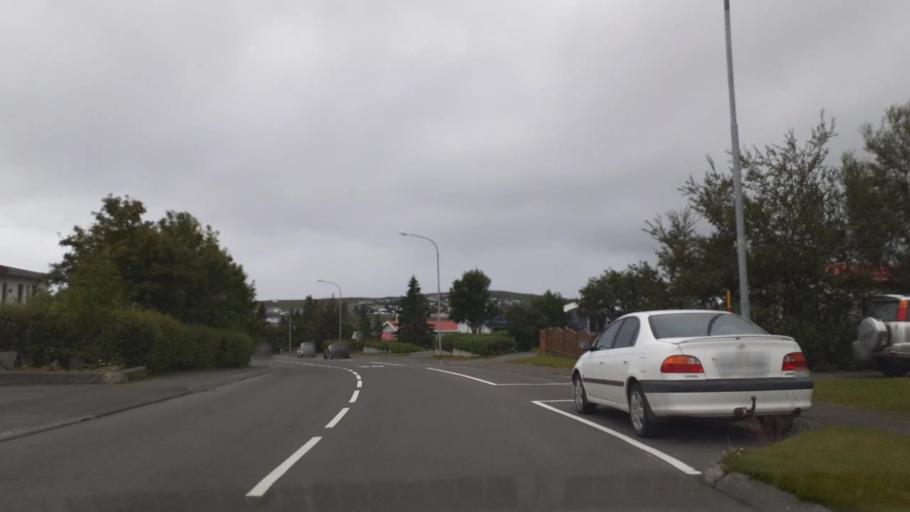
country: IS
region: Northeast
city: Husavik
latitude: 66.0390
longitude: -17.3350
